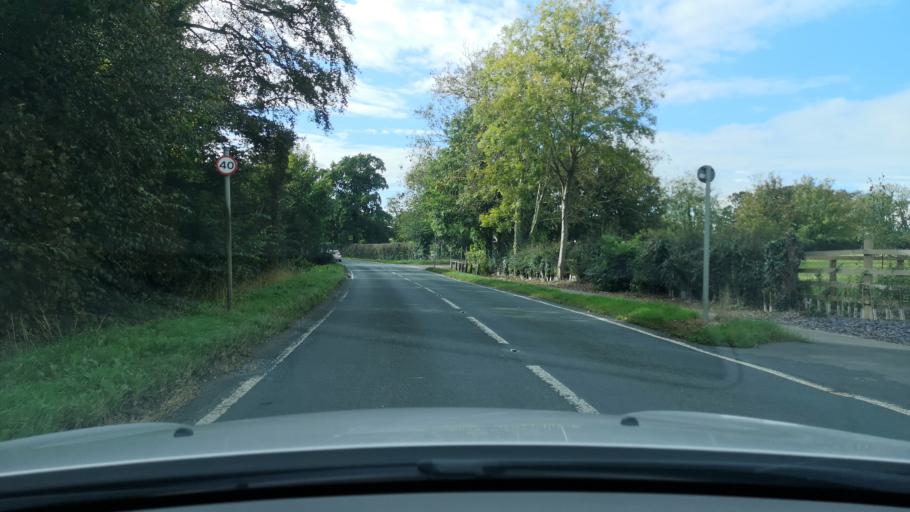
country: GB
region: England
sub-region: East Riding of Yorkshire
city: Hornsea
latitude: 53.9109
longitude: -0.1890
